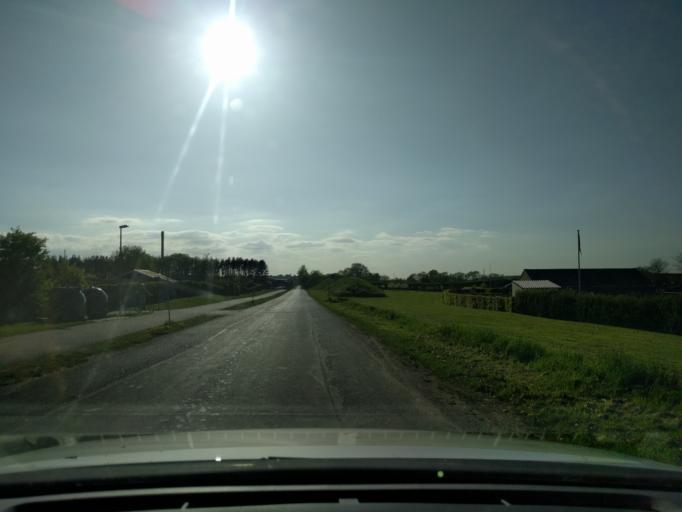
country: DK
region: South Denmark
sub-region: Kerteminde Kommune
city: Kerteminde
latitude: 55.4630
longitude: 10.6603
